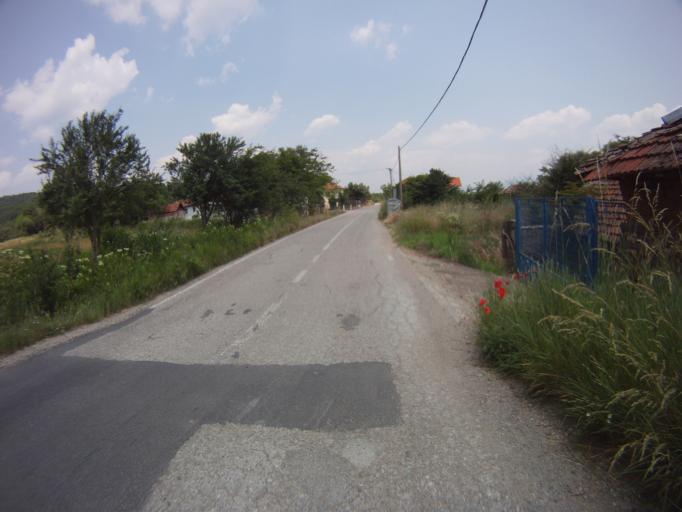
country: RS
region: Central Serbia
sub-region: Nisavski Okrug
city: Gadzin Han
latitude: 43.2011
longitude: 21.9582
